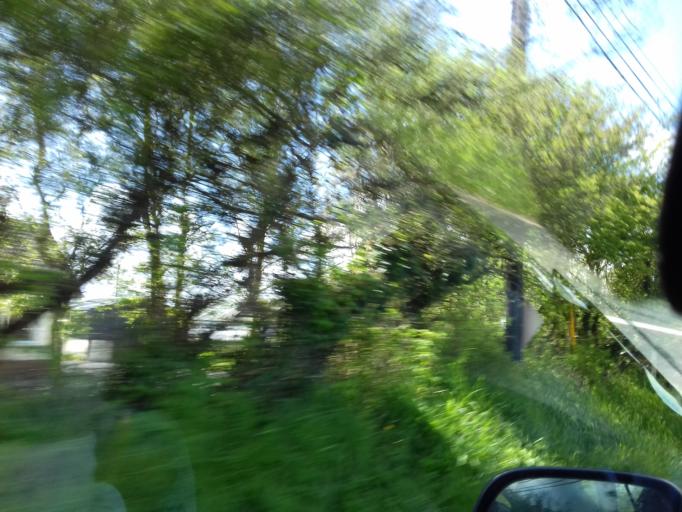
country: IE
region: Leinster
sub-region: Loch Garman
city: Castlebridge
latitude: 52.3913
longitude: -6.4036
